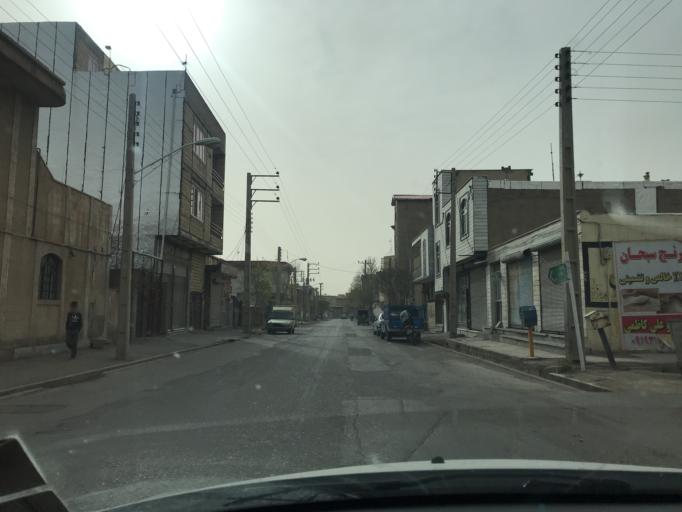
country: IR
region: Qazvin
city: Takestan
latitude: 36.0687
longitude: 49.6877
